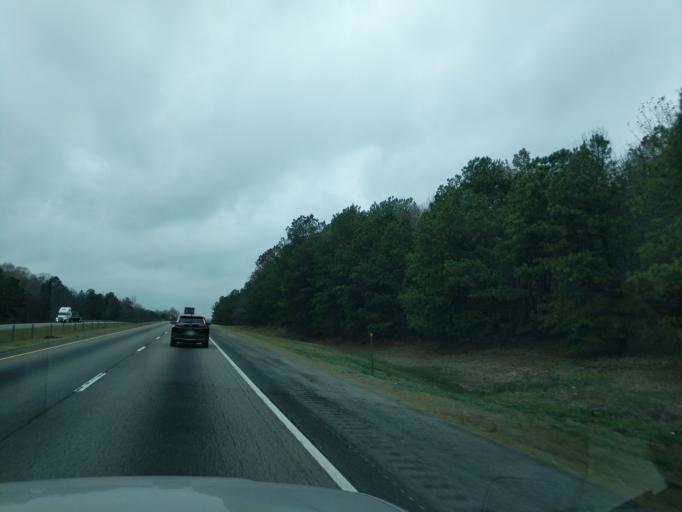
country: US
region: Georgia
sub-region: Barrow County
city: Auburn
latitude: 34.0883
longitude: -83.8401
